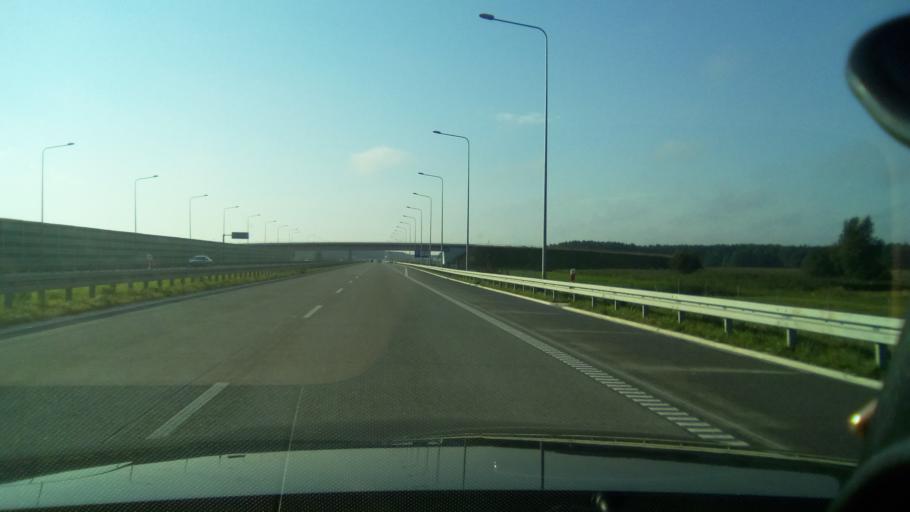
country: PL
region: Silesian Voivodeship
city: Wozniki
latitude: 50.5801
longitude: 19.0471
